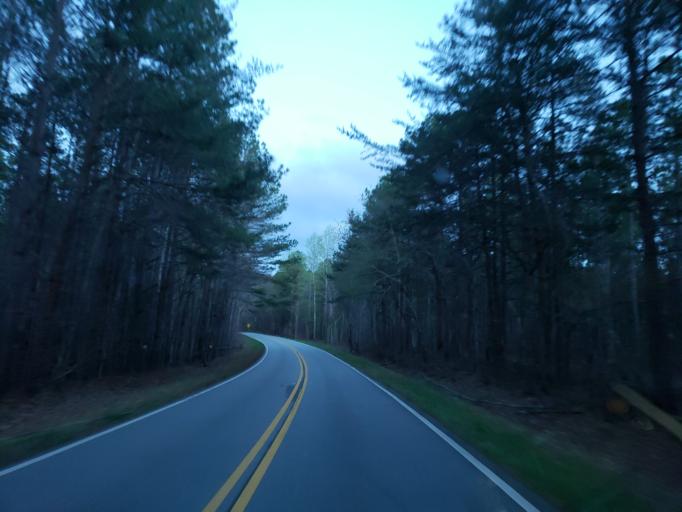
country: US
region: Georgia
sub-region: Paulding County
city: Dallas
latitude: 34.0020
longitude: -84.9182
